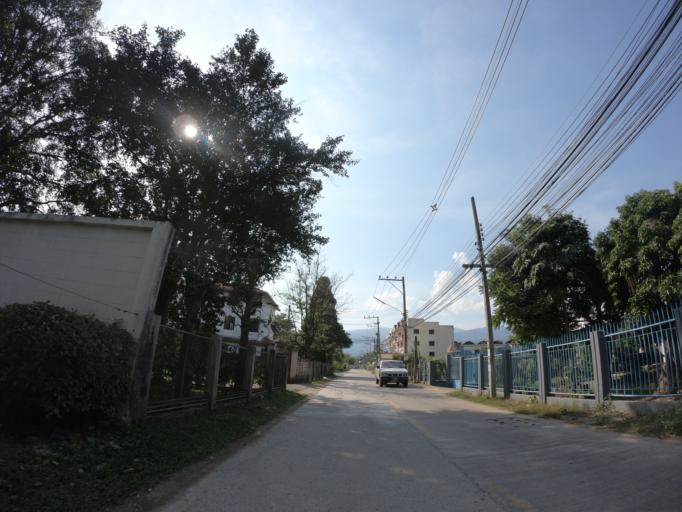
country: TH
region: Chiang Mai
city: Chiang Mai
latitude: 18.8232
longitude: 98.9830
